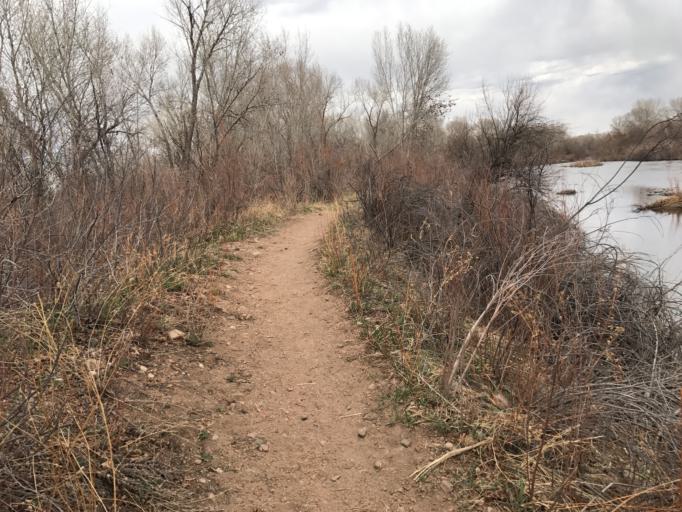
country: US
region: Colorado
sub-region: Douglas County
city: Roxborough Park
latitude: 39.5064
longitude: -105.0850
